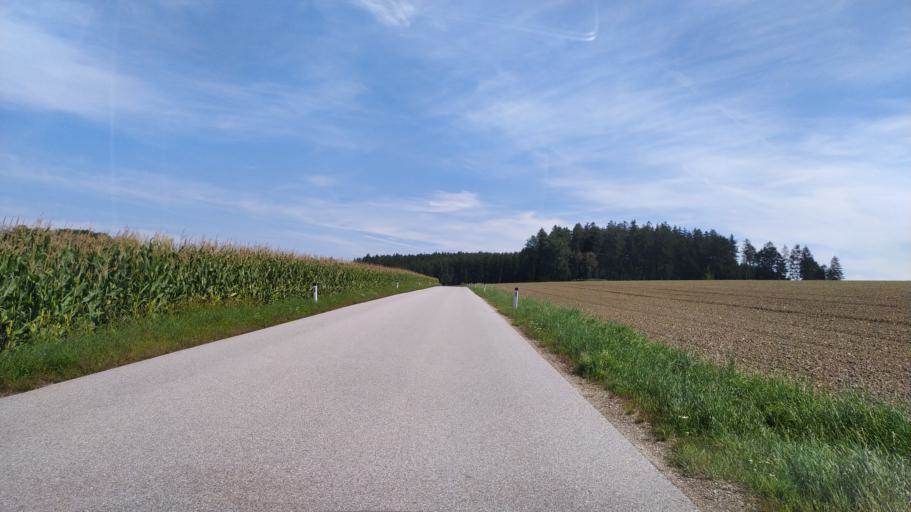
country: AT
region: Lower Austria
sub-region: Politischer Bezirk Amstetten
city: Wolfsbach
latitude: 48.1094
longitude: 14.6854
